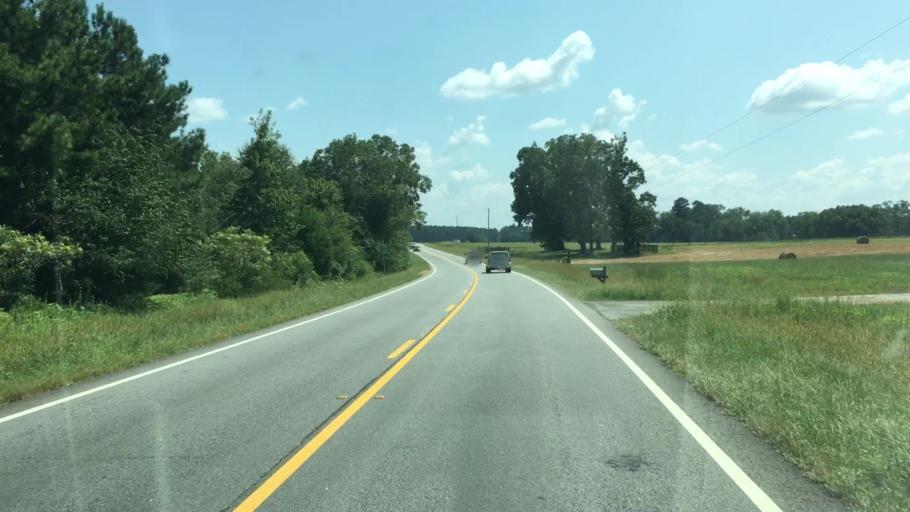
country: US
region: Georgia
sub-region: Oconee County
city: Watkinsville
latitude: 33.8020
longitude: -83.4268
